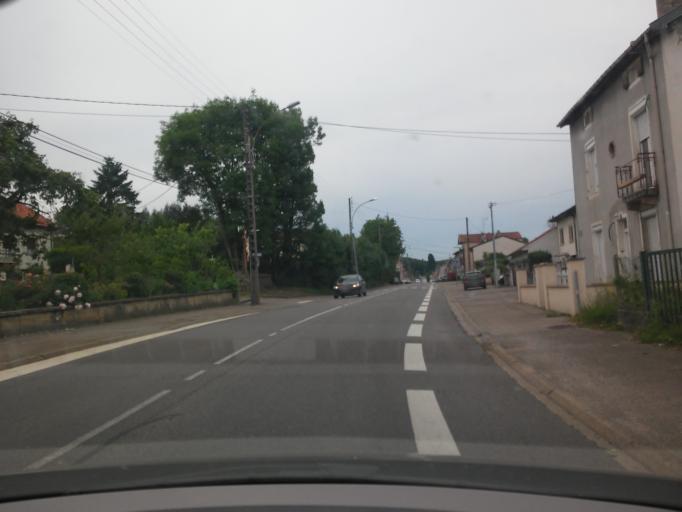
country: FR
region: Lorraine
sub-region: Departement de Meurthe-et-Moselle
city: Montauville
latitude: 48.9006
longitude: 6.0273
